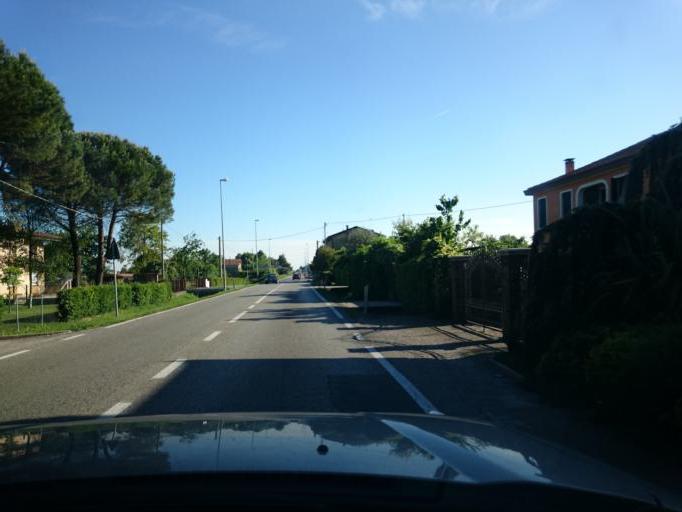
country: IT
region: Veneto
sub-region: Provincia di Venezia
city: Caselle
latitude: 45.4989
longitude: 12.0089
